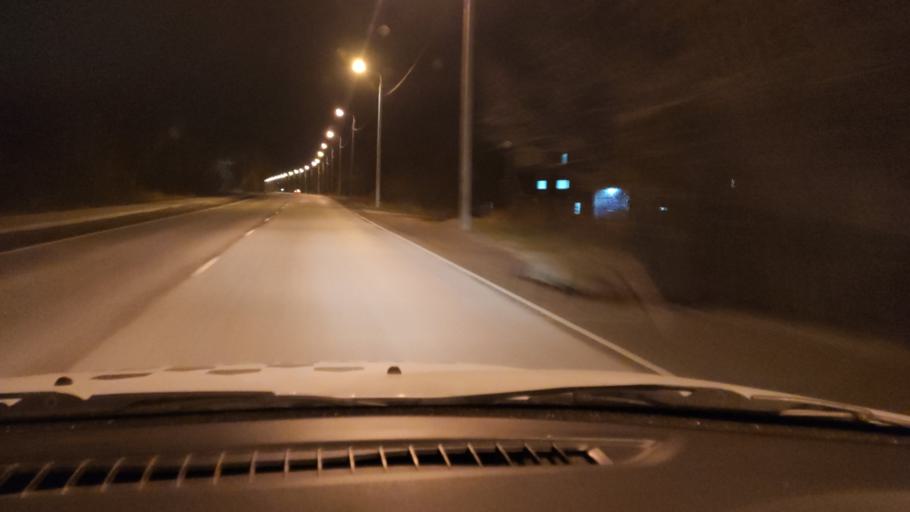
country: RU
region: Perm
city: Kondratovo
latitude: 57.9878
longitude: 56.1343
